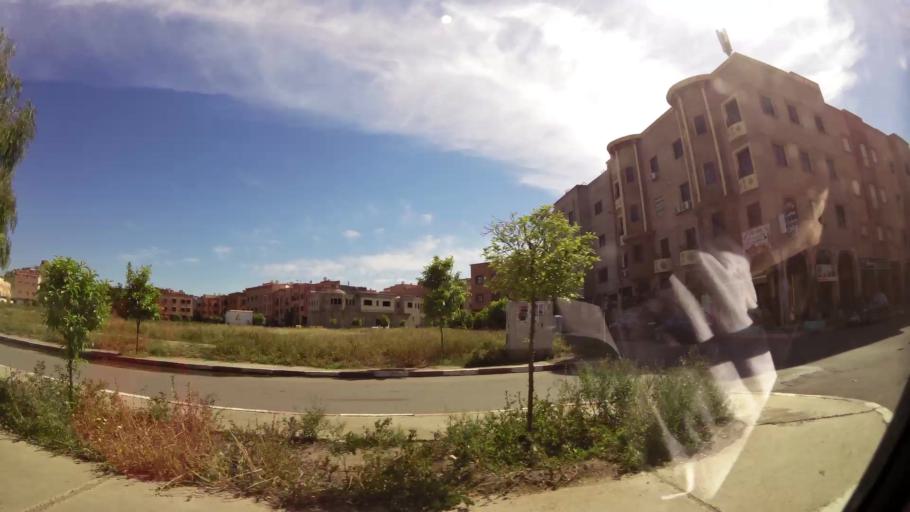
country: MA
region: Marrakech-Tensift-Al Haouz
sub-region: Marrakech
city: Marrakesh
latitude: 31.6689
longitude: -8.0252
